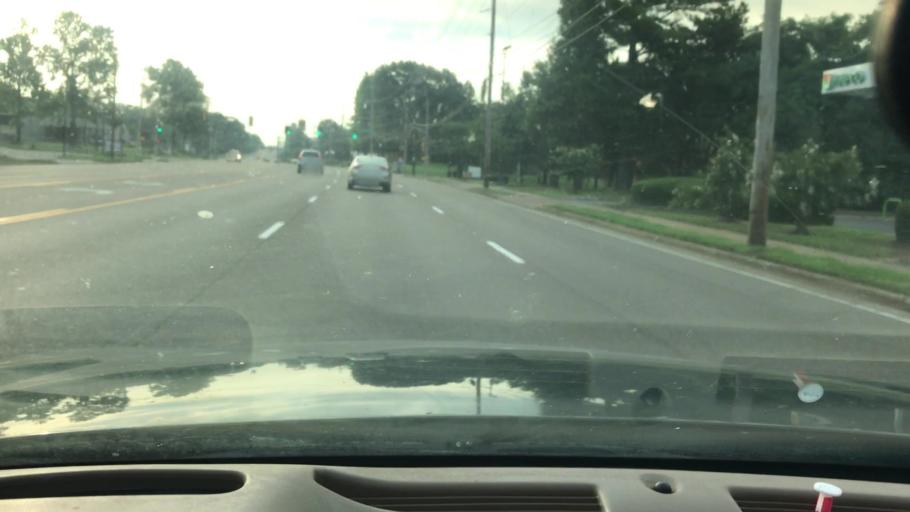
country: US
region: Tennessee
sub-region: Shelby County
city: Bartlett
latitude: 35.2046
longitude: -89.8588
